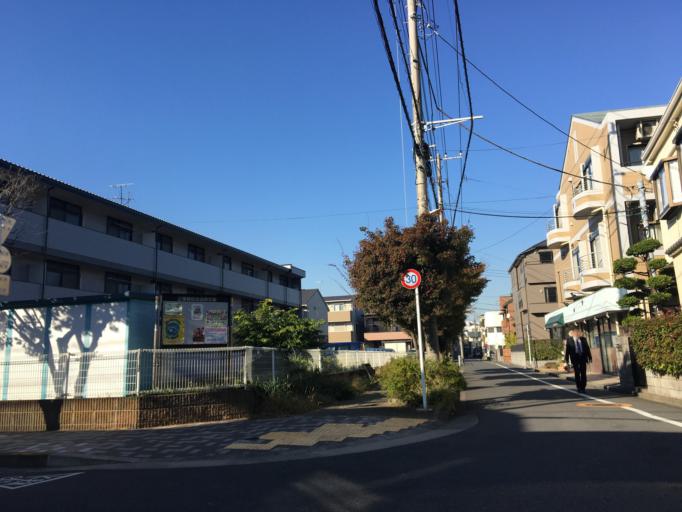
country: JP
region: Tokyo
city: Urayasu
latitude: 35.7113
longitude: 139.9039
